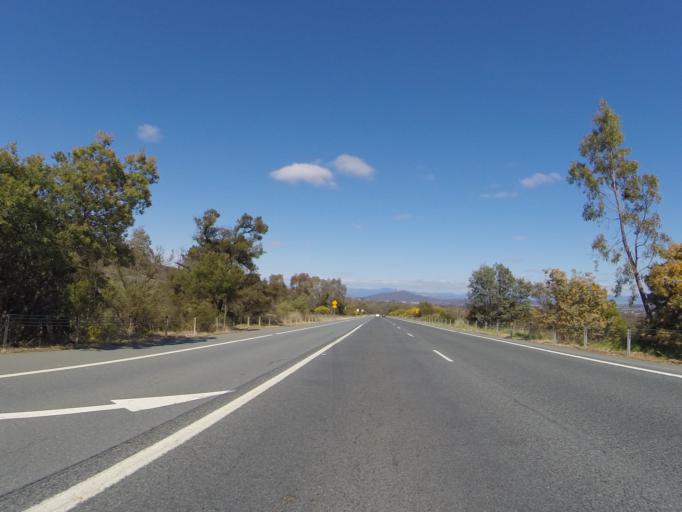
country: AU
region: Australian Capital Territory
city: Kaleen
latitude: -35.2172
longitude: 149.1829
